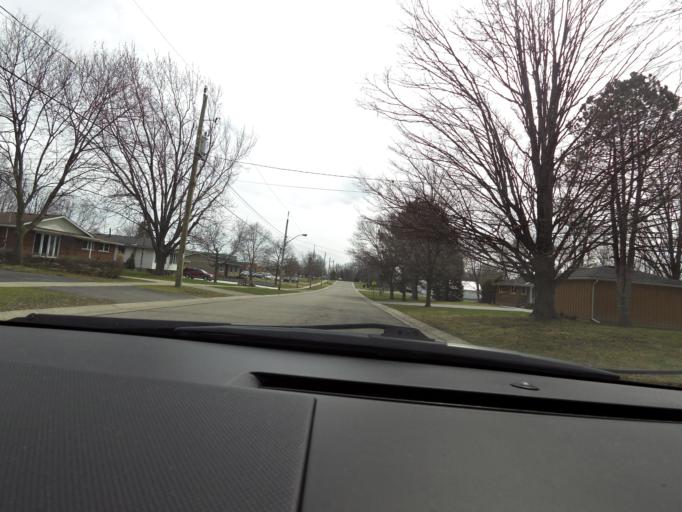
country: CA
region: Ontario
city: Ancaster
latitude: 42.9460
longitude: -79.8538
